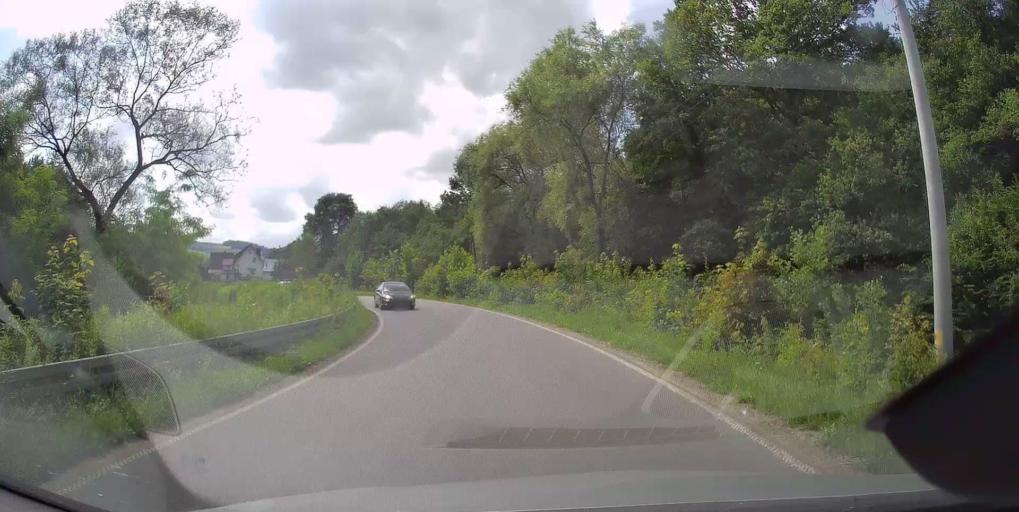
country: PL
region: Lesser Poland Voivodeship
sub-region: Powiat nowosadecki
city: Korzenna
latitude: 49.7421
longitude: 20.7681
